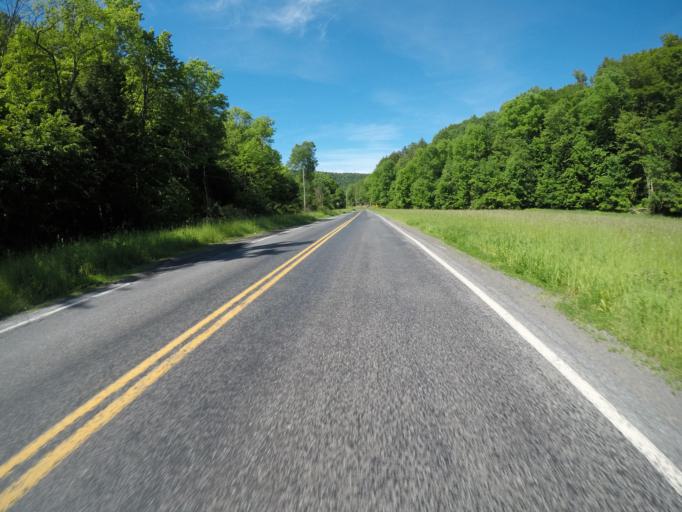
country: US
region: New York
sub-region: Delaware County
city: Delhi
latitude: 42.2050
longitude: -74.9551
